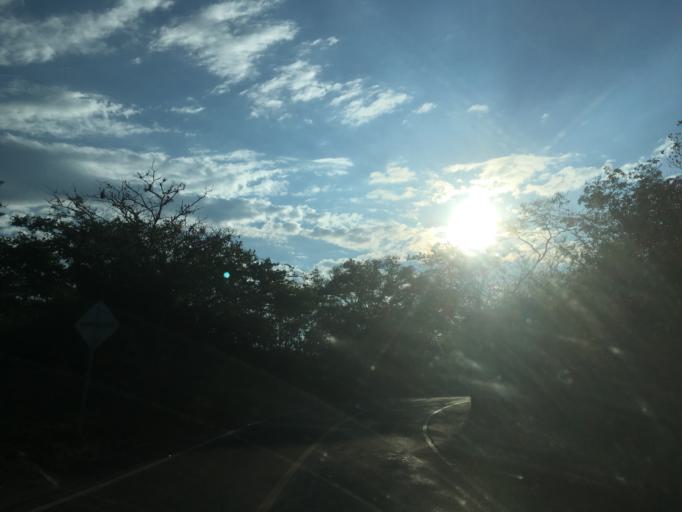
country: CO
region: Santander
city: Barichara
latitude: 6.6390
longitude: -73.2052
